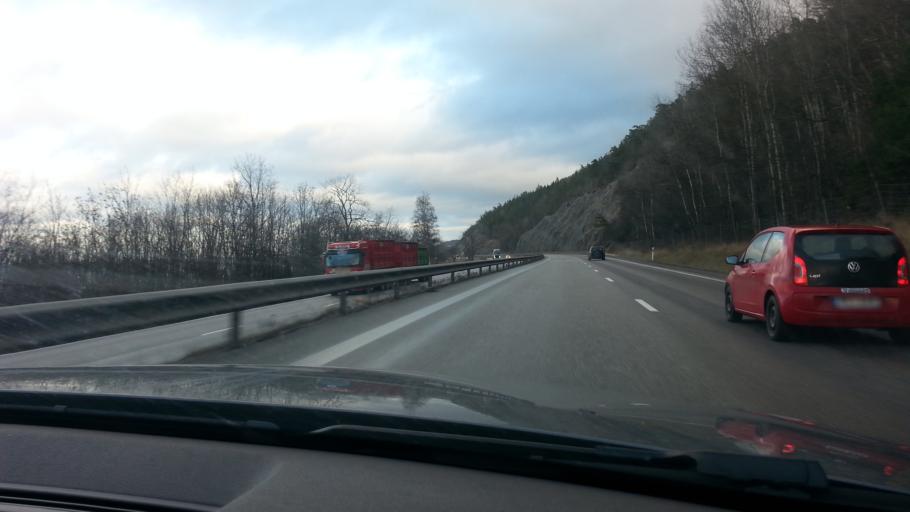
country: SE
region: Joenkoeping
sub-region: Jonkopings Kommun
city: Kaxholmen
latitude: 57.8898
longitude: 14.2868
